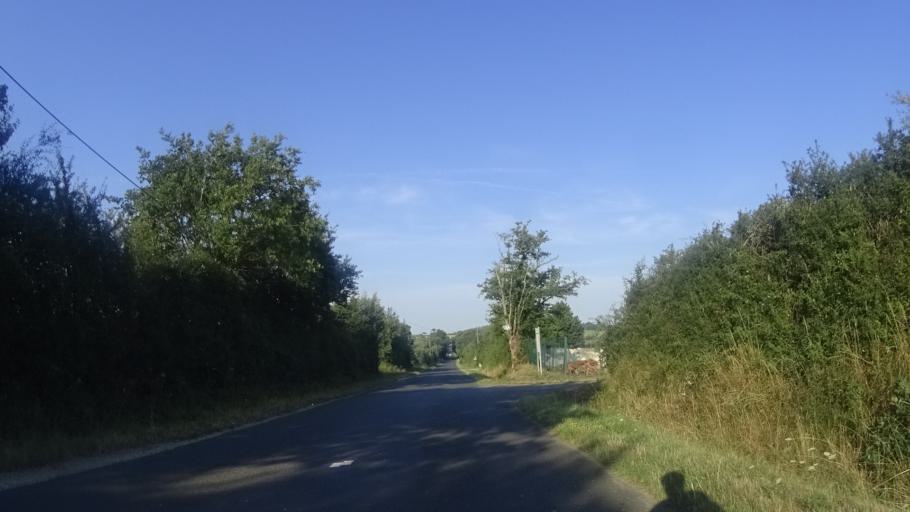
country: FR
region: Pays de la Loire
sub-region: Departement de la Loire-Atlantique
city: Riaille
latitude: 47.4945
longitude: -1.3227
